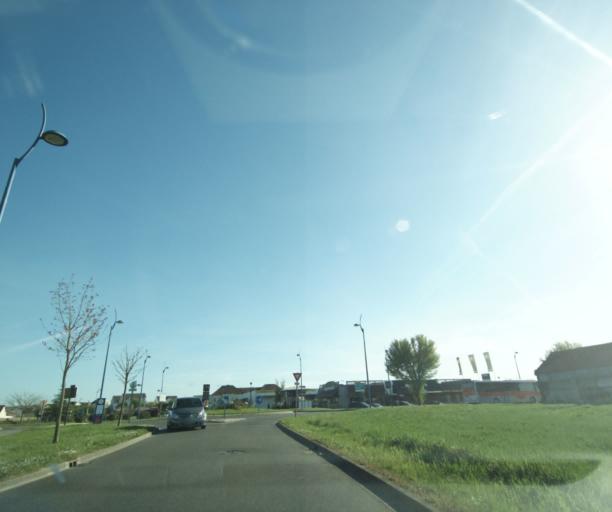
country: FR
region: Ile-de-France
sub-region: Departement de Seine-et-Marne
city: Nangis
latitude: 48.5569
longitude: 3.0049
